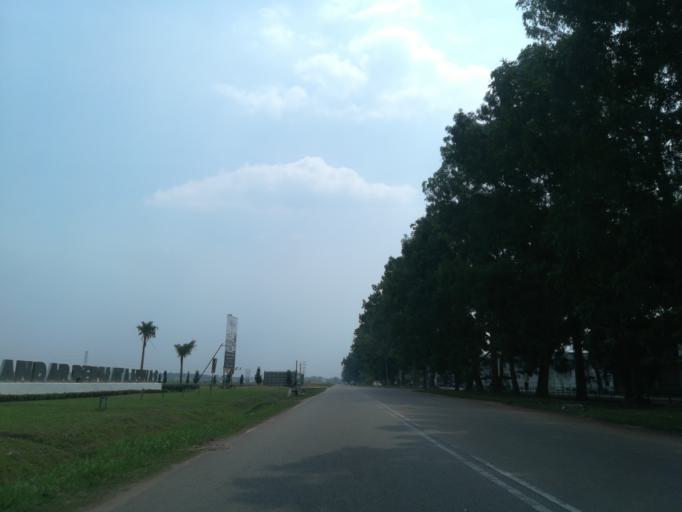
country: MY
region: Penang
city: Tasek Glugor
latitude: 5.4445
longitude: 100.5378
